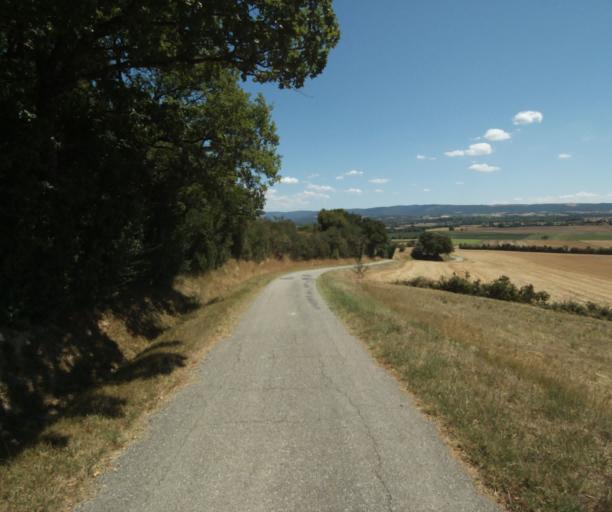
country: FR
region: Midi-Pyrenees
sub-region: Departement de la Haute-Garonne
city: Saint-Felix-Lauragais
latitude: 43.4605
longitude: 1.9213
